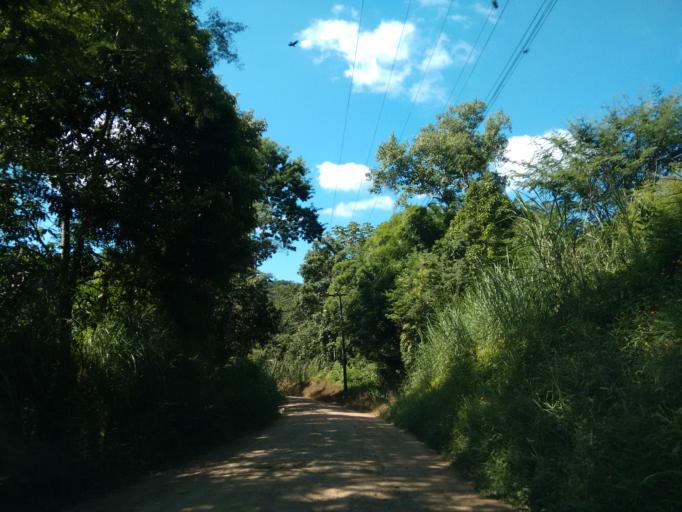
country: BR
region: Santa Catarina
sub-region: Indaial
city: Indaial
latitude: -26.9413
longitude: -49.1788
